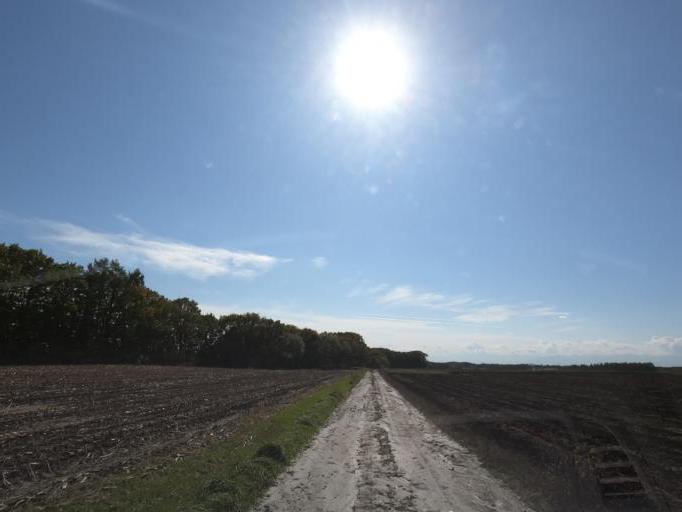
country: JP
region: Hokkaido
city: Otofuke
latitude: 43.2367
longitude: 143.2613
